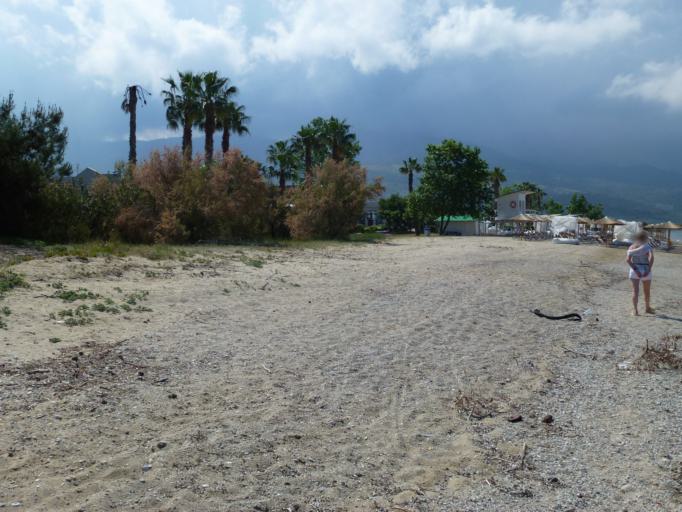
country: GR
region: East Macedonia and Thrace
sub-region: Nomos Kavalas
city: Prinos
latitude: 40.7563
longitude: 24.5610
